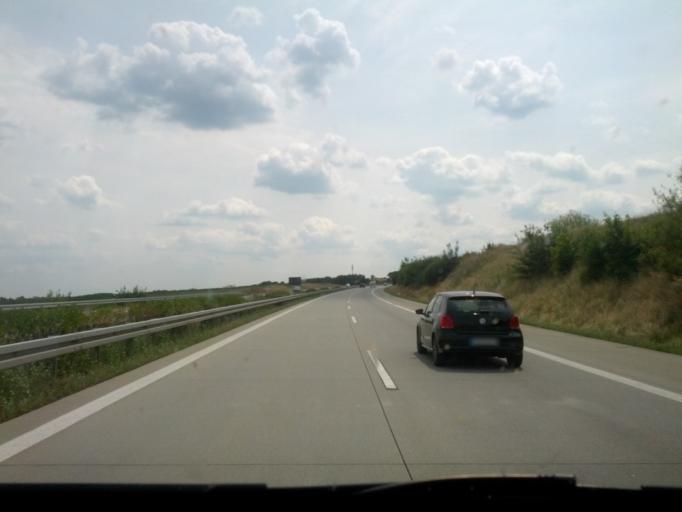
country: DE
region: Saxony
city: Dohna
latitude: 50.9307
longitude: 13.8887
